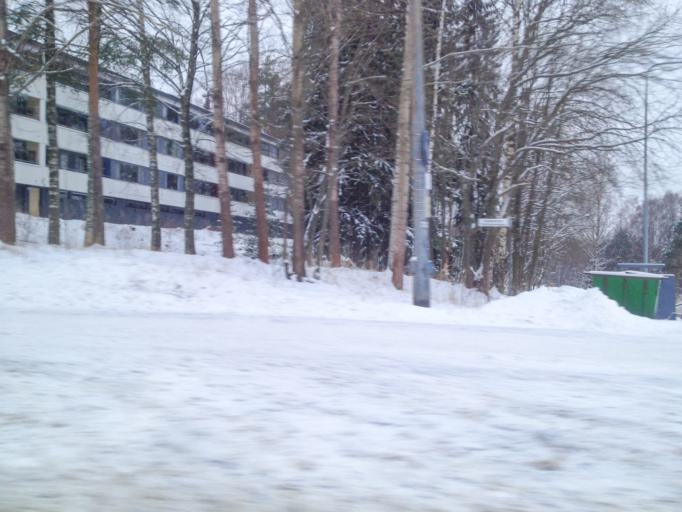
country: FI
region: Uusimaa
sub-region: Helsinki
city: Vantaa
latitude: 60.2220
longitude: 25.1339
